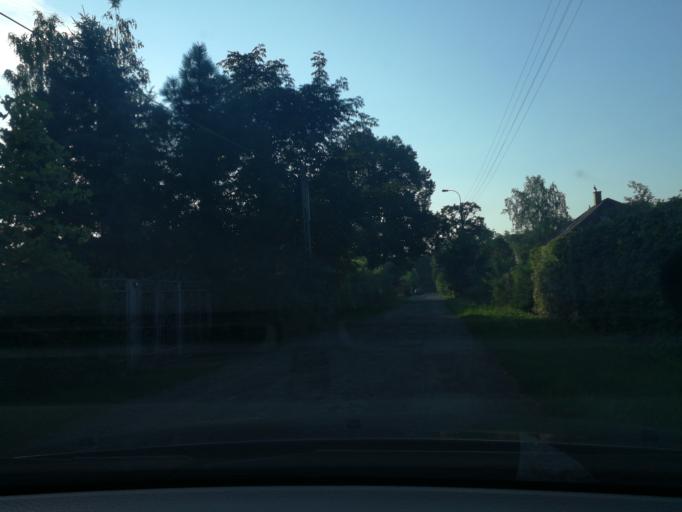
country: PL
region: Masovian Voivodeship
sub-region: Powiat pruszkowski
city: Brwinow
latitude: 52.1357
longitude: 20.7129
